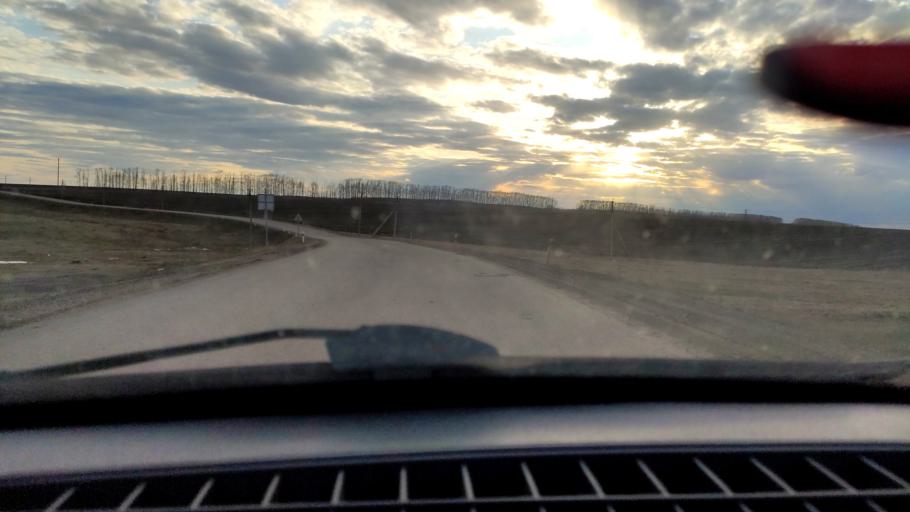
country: RU
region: Bashkortostan
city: Tolbazy
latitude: 53.9886
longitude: 55.8061
